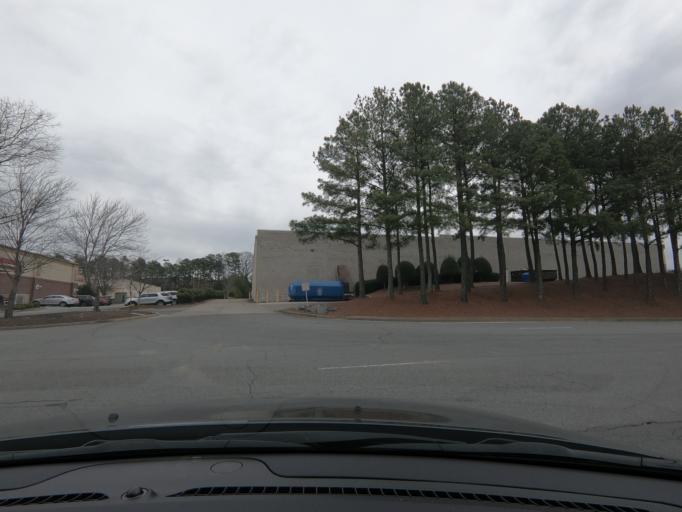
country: US
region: Georgia
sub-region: Cobb County
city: Kennesaw
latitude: 34.0124
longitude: -84.5724
